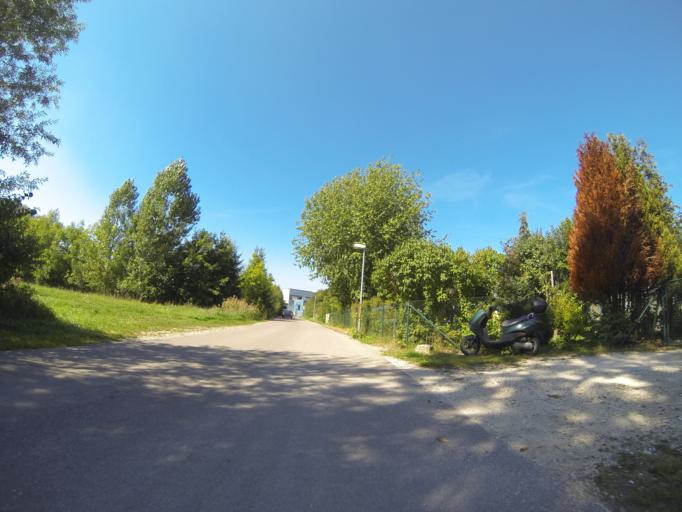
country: DE
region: Baden-Wuerttemberg
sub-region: Tuebingen Region
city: Erbach
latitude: 48.3243
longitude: 9.9032
